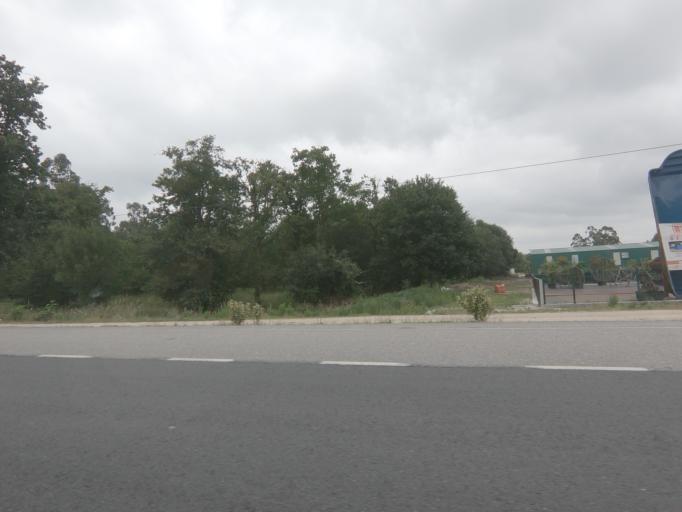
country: PT
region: Viana do Castelo
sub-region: Vila Nova de Cerveira
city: Vila Nova de Cerveira
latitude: 41.9535
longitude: -8.7607
